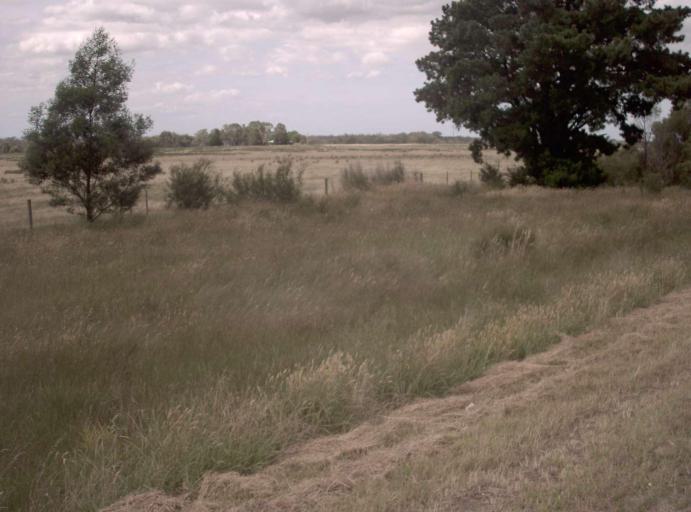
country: AU
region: Victoria
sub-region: Wellington
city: Sale
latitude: -38.1653
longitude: 147.0447
